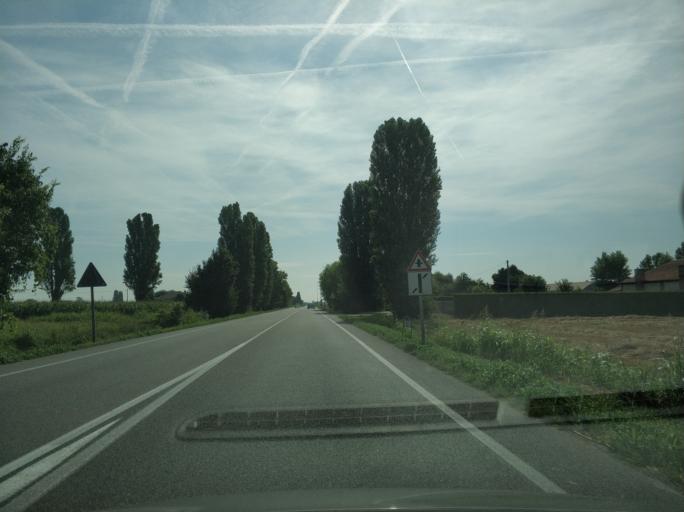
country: IT
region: Veneto
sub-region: Provincia di Padova
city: Arre
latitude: 45.2112
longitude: 11.9402
